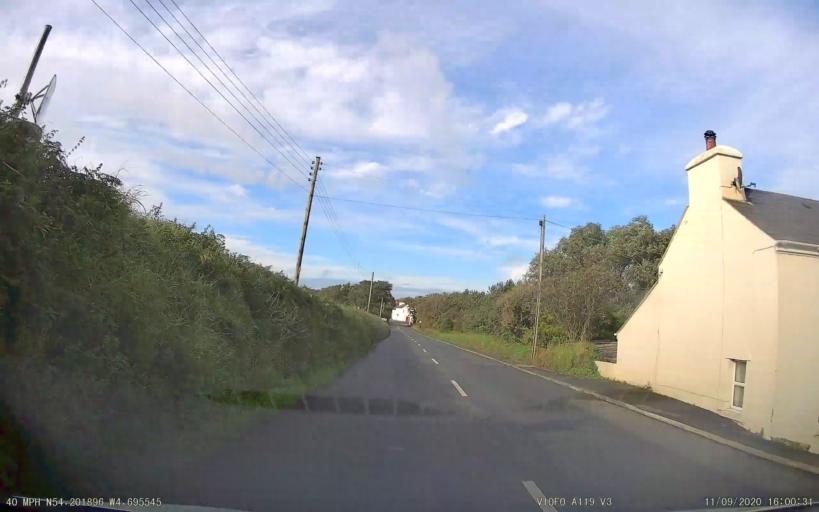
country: IM
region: Port Erin
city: Port Erin
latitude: 54.2019
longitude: -4.6955
